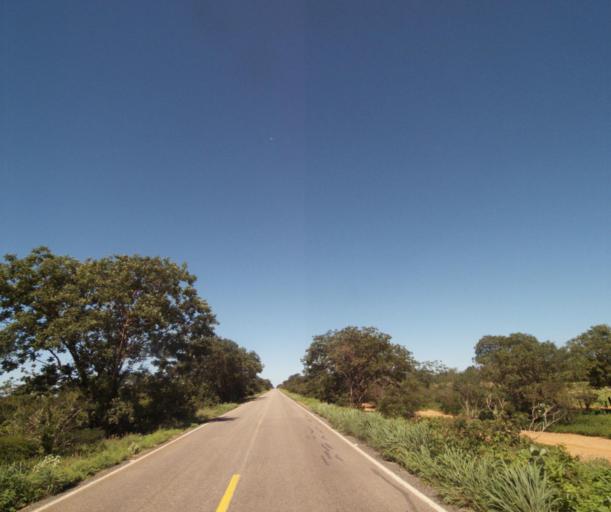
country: BR
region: Bahia
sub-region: Palmas De Monte Alto
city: Palmas de Monte Alto
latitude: -14.2608
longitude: -43.3012
